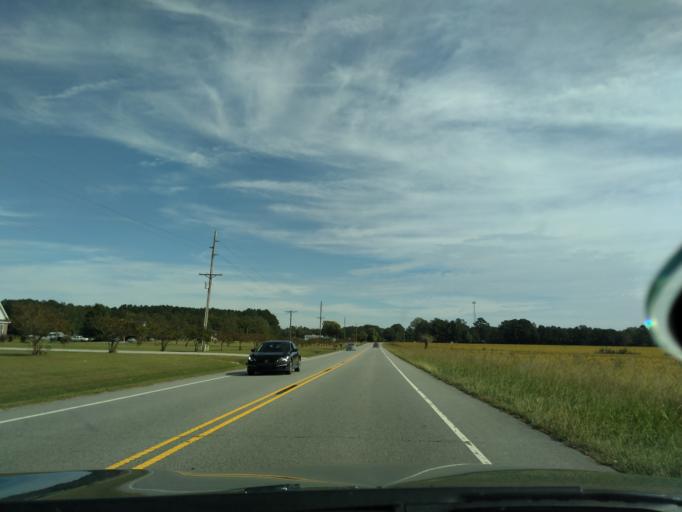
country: US
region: North Carolina
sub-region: Beaufort County
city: River Road
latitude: 35.5177
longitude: -76.9222
